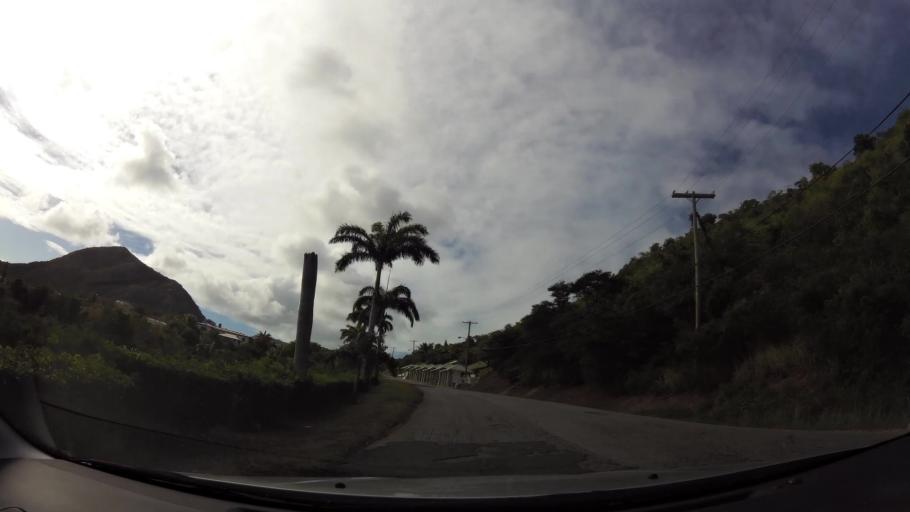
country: AG
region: Saint Paul
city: Liberta
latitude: 17.0297
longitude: -61.7852
